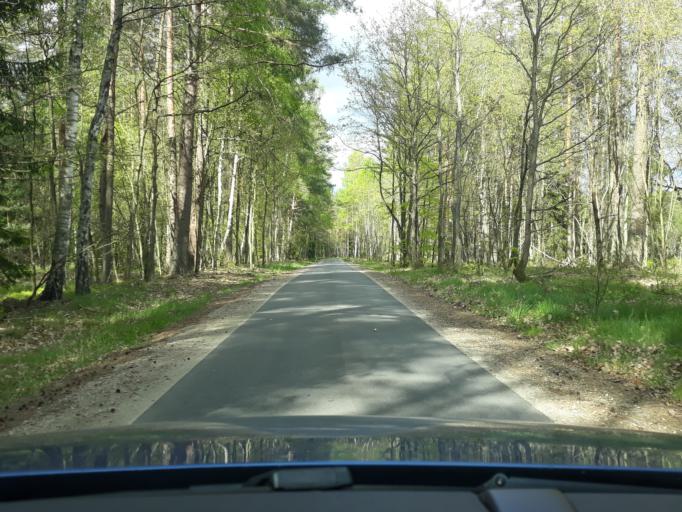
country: PL
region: Pomeranian Voivodeship
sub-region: Powiat czluchowski
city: Czluchow
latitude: 53.7247
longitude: 17.3358
